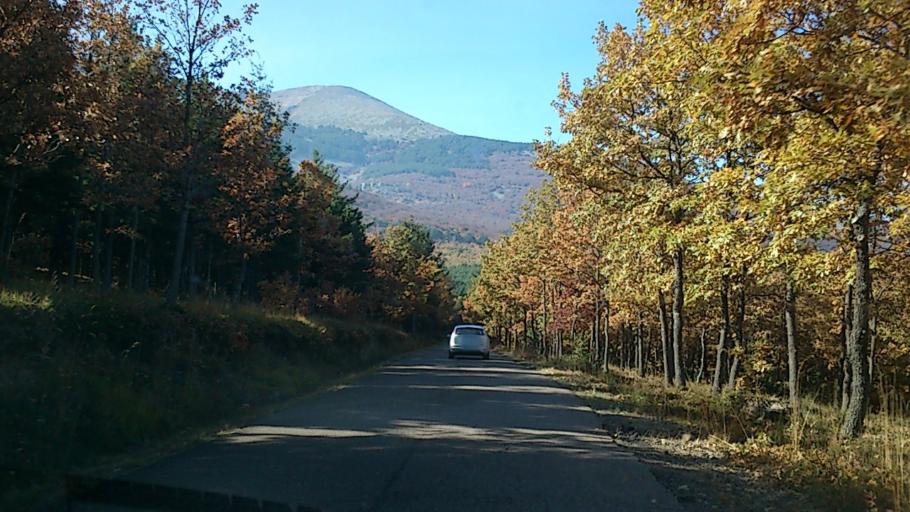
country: ES
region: Aragon
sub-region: Provincia de Zaragoza
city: Litago
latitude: 41.8065
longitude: -1.7963
